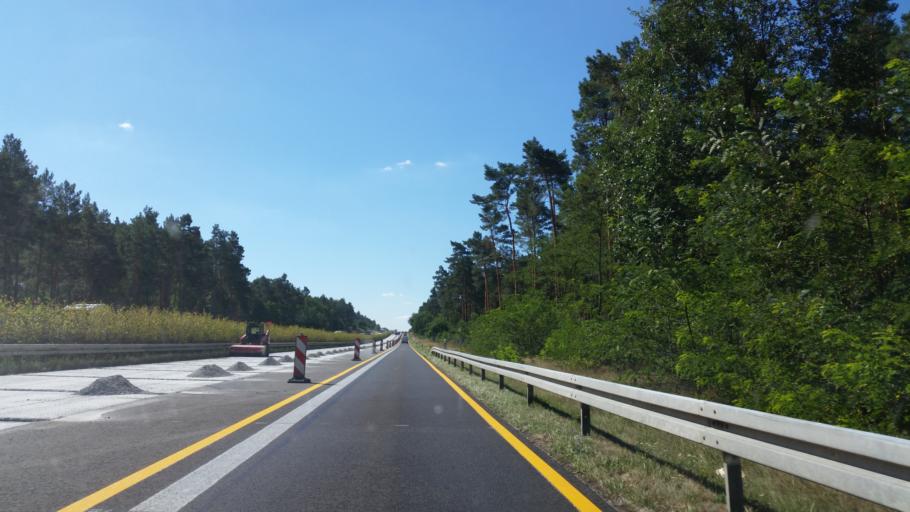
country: DE
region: Brandenburg
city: Teupitz
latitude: 52.0938
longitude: 13.6479
